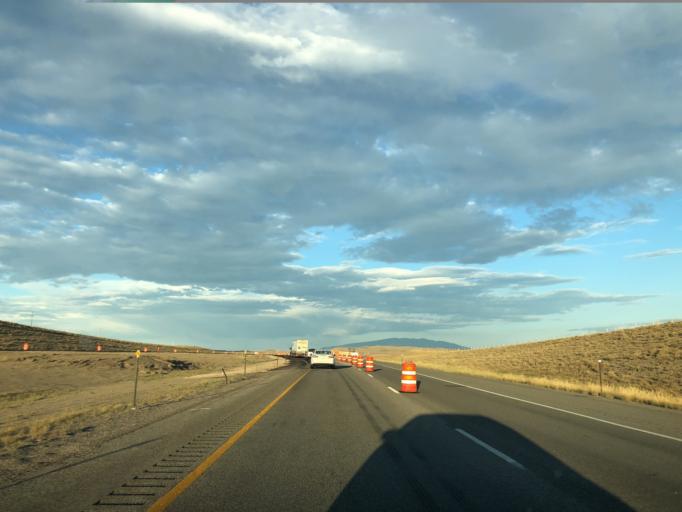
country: US
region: Wyoming
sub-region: Carbon County
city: Rawlins
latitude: 41.7571
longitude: -106.9784
